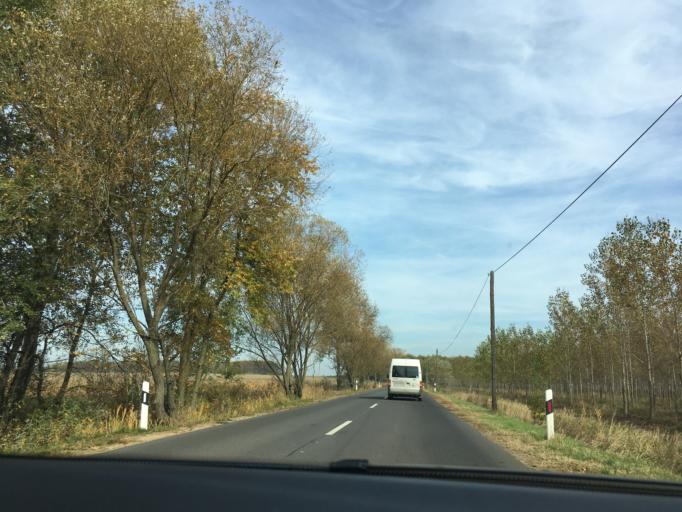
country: HU
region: Szabolcs-Szatmar-Bereg
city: Nagykallo
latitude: 47.8447
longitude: 21.7787
